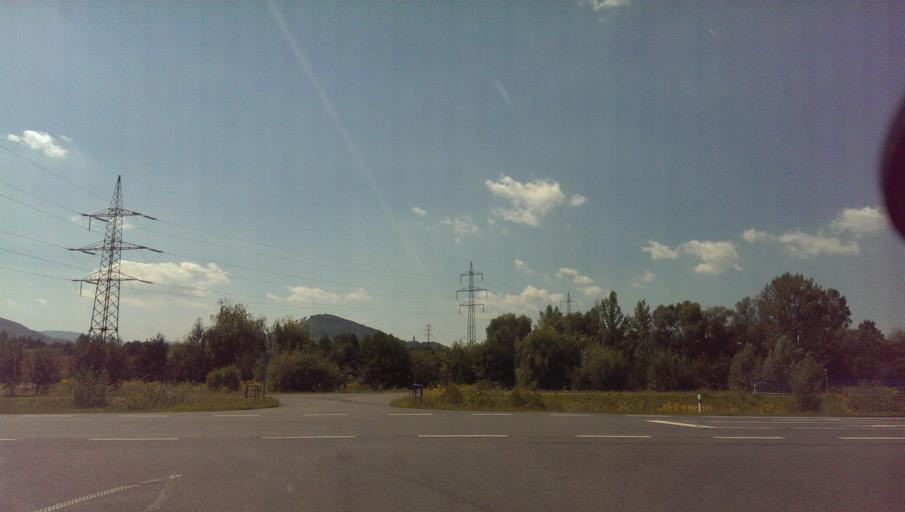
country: CZ
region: Moravskoslezsky
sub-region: Okres Novy Jicin
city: Pribor
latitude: 49.6217
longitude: 18.1496
